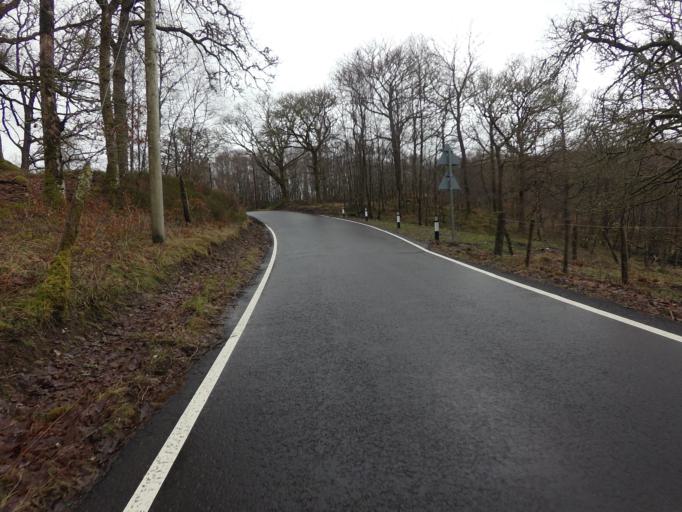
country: GB
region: Scotland
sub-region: West Dunbartonshire
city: Balloch
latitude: 56.1941
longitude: -4.5154
